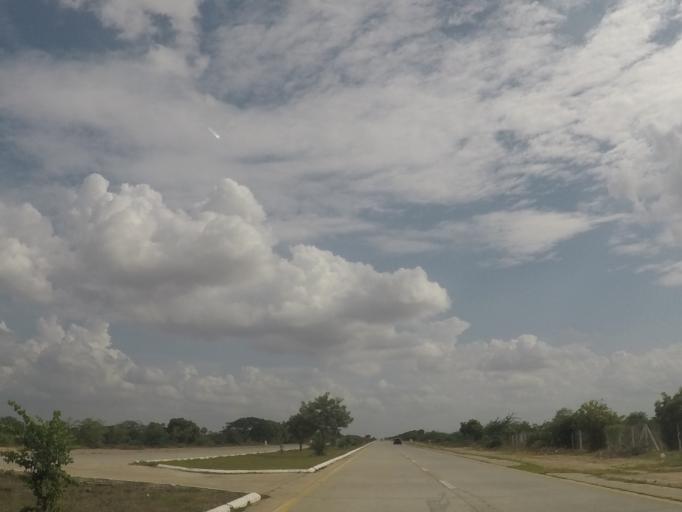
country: MM
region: Mandalay
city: Kyaukse
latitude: 21.4989
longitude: 95.9320
